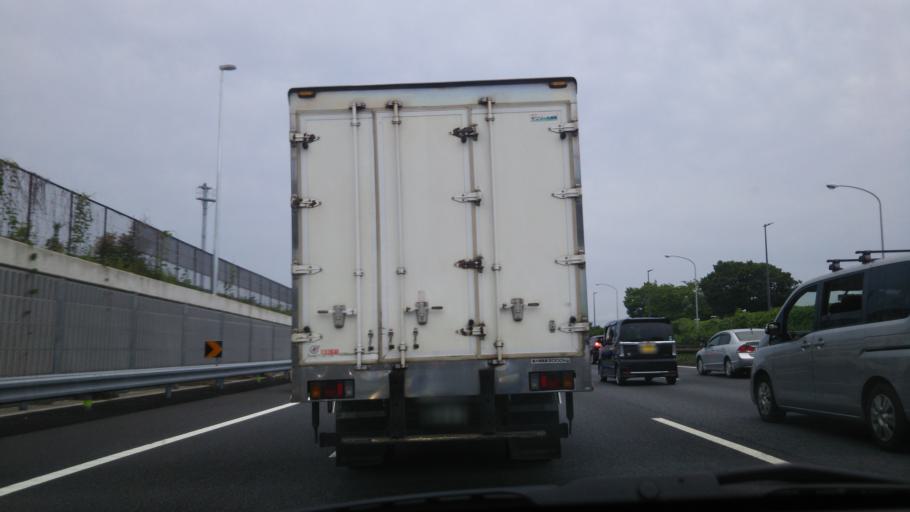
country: JP
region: Kanagawa
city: Atsugi
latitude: 35.4315
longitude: 139.3999
